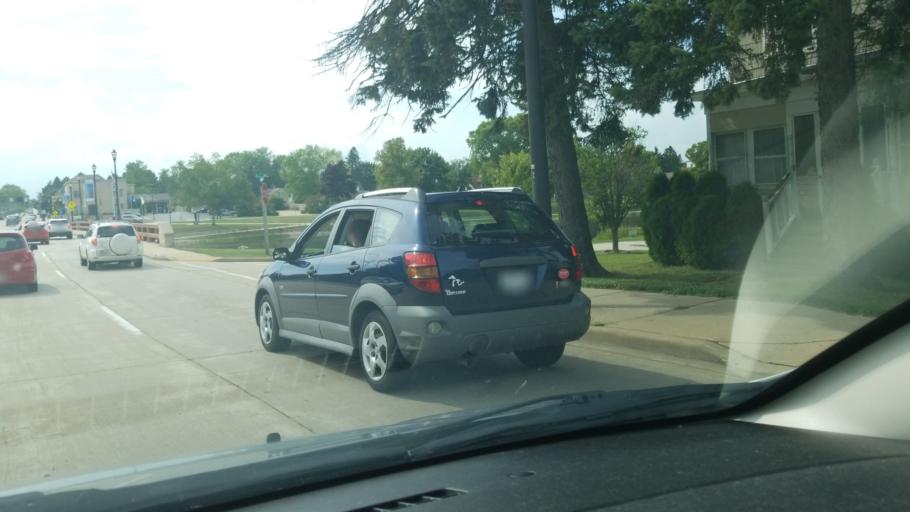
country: US
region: Wisconsin
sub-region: Ozaukee County
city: Grafton
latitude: 43.3200
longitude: -87.9484
